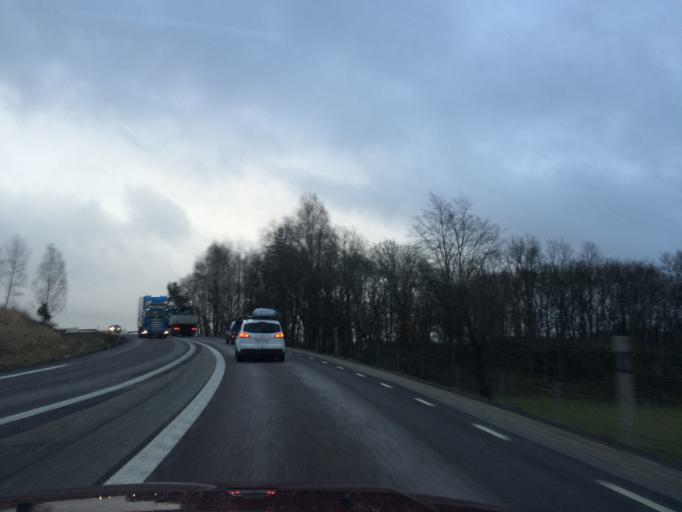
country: SE
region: Halland
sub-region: Kungsbacka Kommun
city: Kungsbacka
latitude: 57.5115
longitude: 12.0495
